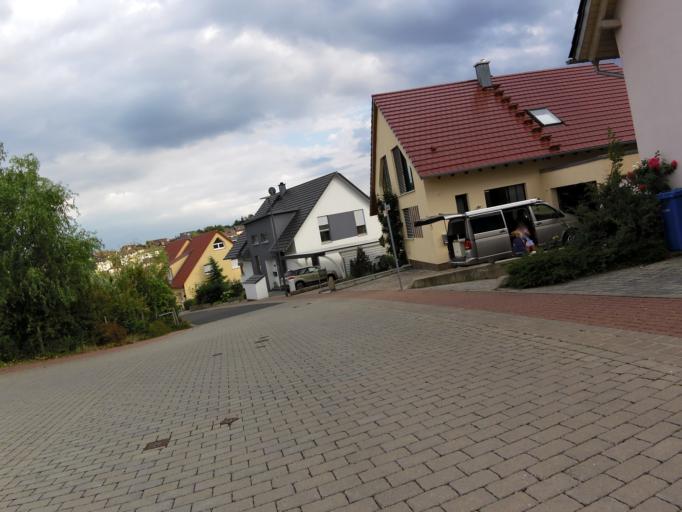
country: DE
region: Bavaria
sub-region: Regierungsbezirk Unterfranken
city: Hochberg
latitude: 49.7780
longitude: 9.8679
